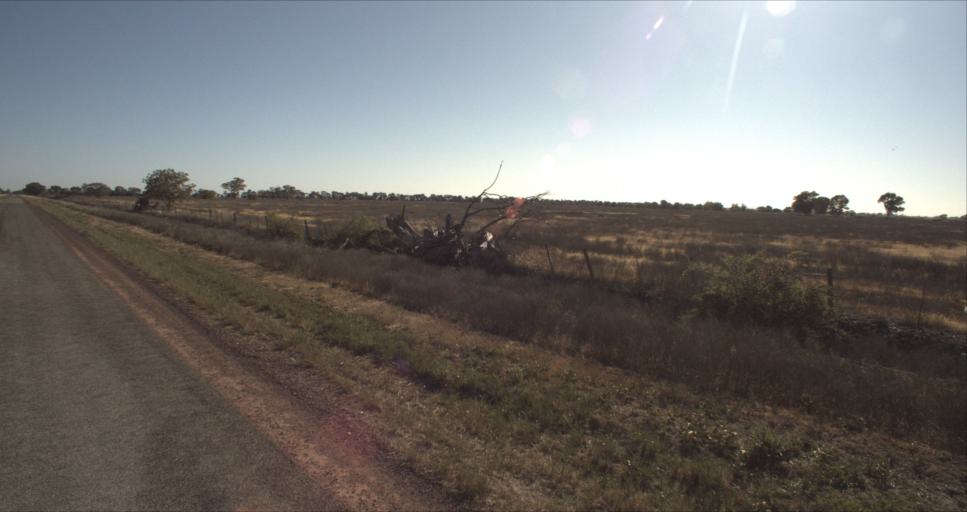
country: AU
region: New South Wales
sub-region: Leeton
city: Leeton
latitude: -34.5863
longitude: 146.2606
